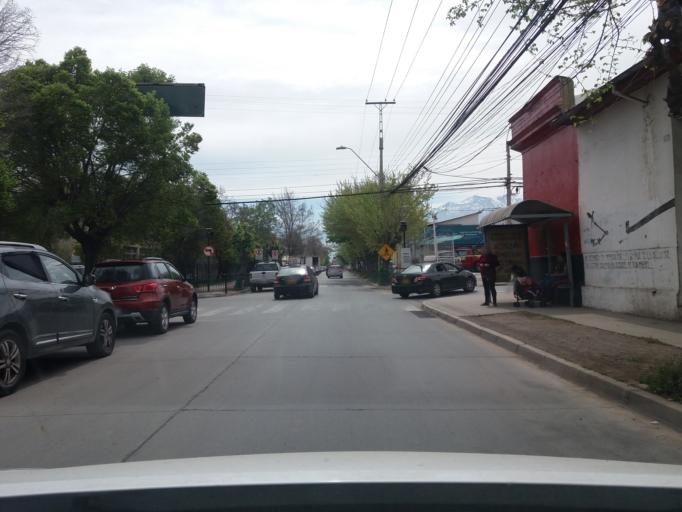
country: CL
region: Valparaiso
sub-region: Provincia de Los Andes
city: Los Andes
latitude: -32.8347
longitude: -70.5937
